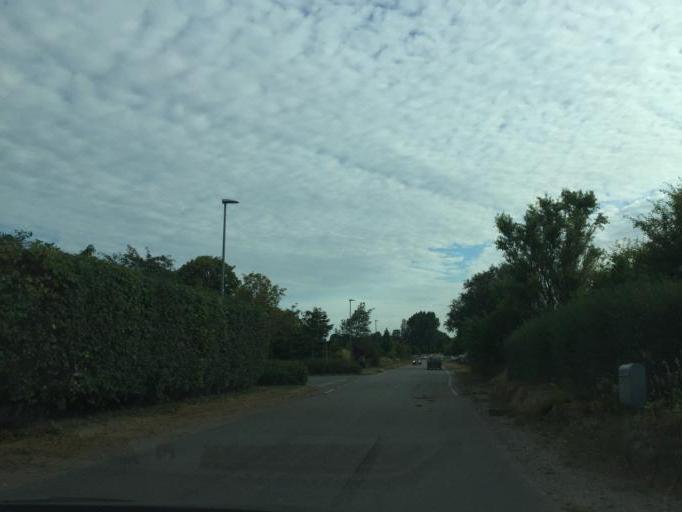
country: DK
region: South Denmark
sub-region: Assens Kommune
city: Assens
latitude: 55.2425
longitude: 9.9643
